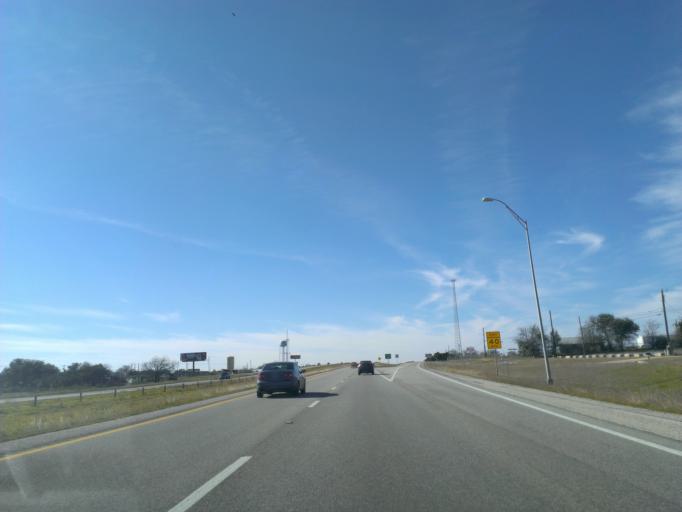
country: US
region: Texas
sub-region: Bell County
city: Nolanville
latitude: 31.0554
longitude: -97.5434
